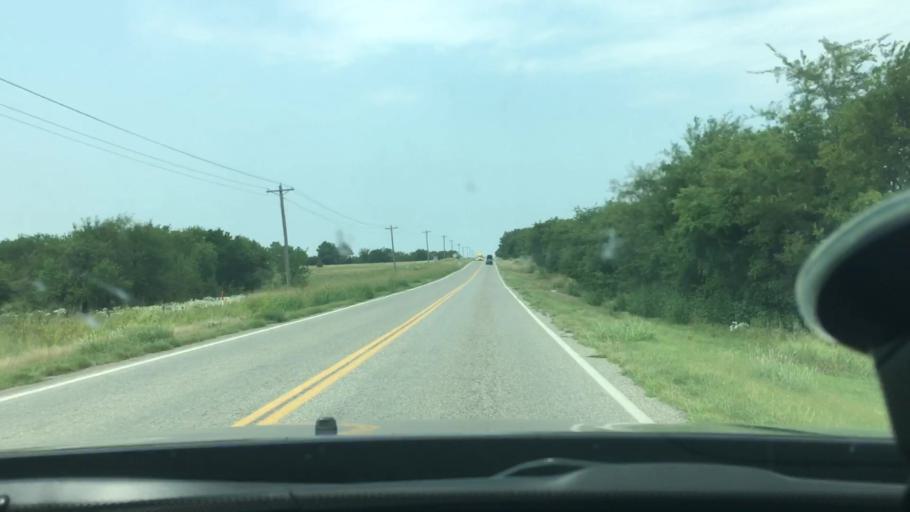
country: US
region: Oklahoma
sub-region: Marshall County
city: Kingston
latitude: 33.9983
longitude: -96.7641
